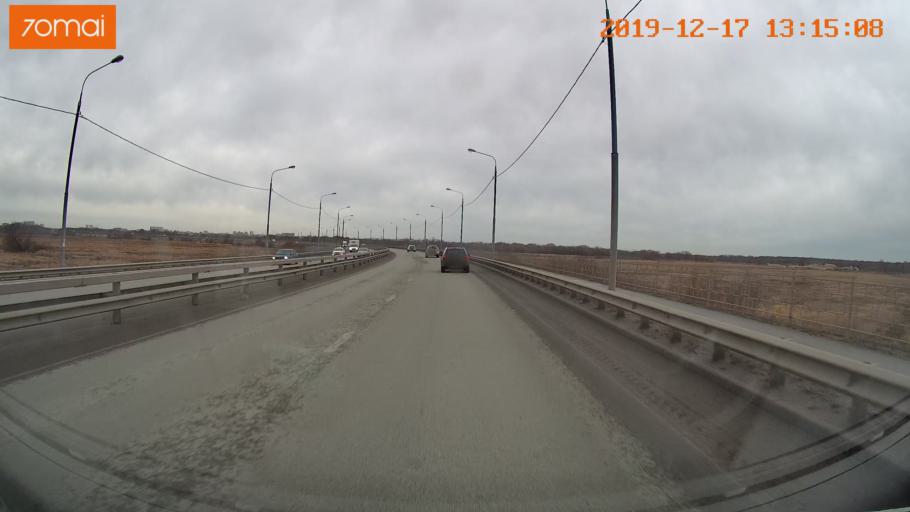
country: RU
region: Rjazan
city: Ryazan'
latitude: 54.6470
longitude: 39.7472
